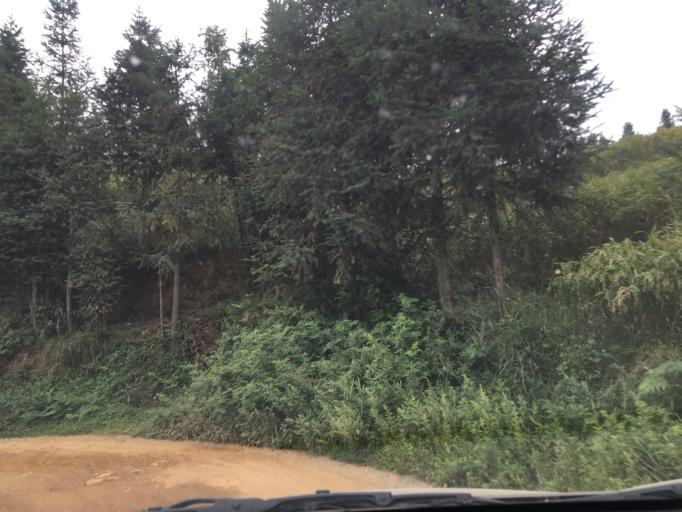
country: CN
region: Guangxi Zhuangzu Zizhiqu
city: Xinzhou
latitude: 25.5437
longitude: 105.5329
